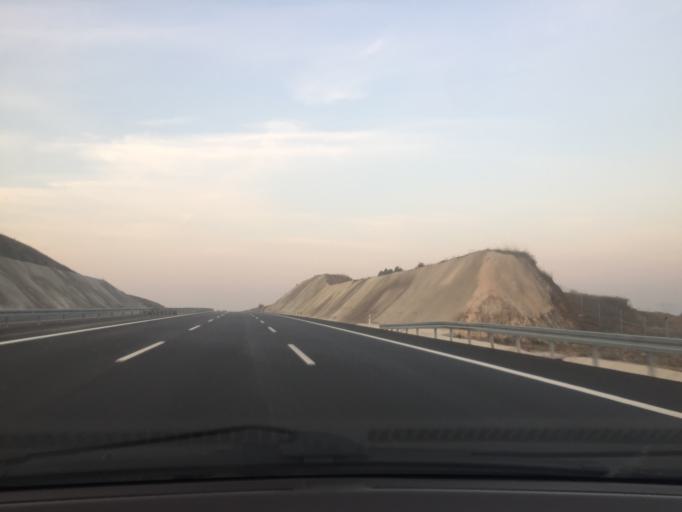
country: TR
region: Bursa
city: Karacabey
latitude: 40.2719
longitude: 28.5022
